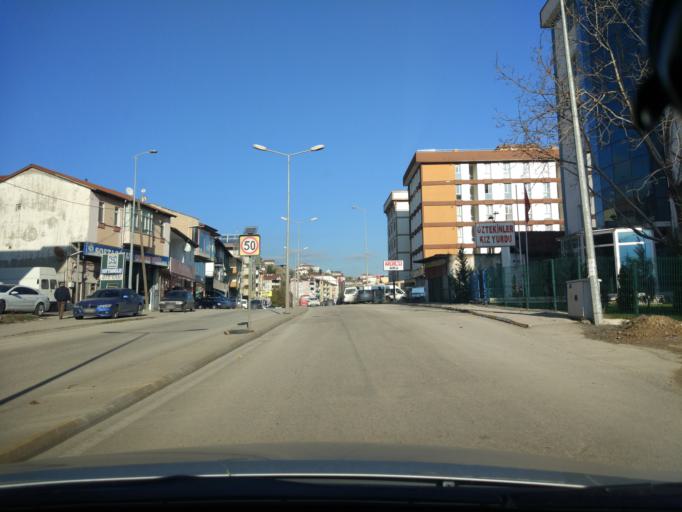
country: TR
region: Karabuk
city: Karabuk
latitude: 41.2091
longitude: 32.6398
